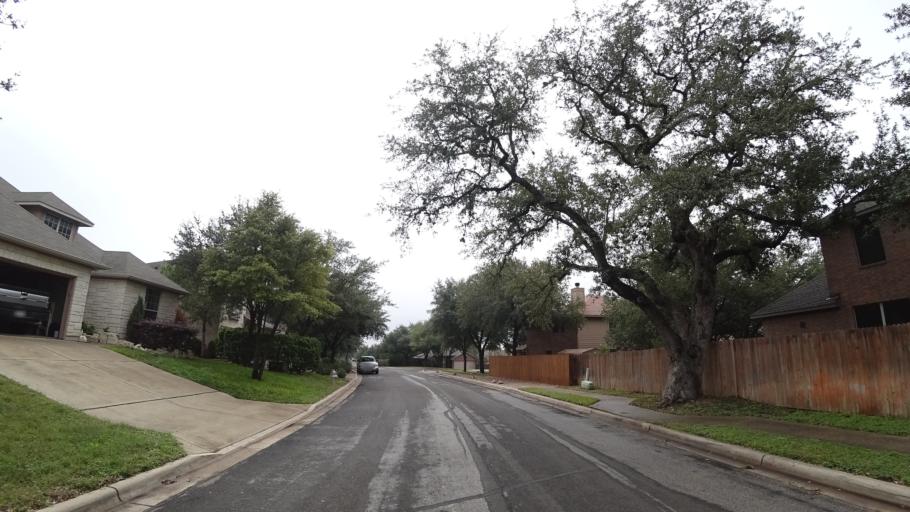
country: US
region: Texas
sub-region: Travis County
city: Shady Hollow
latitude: 30.1909
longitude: -97.8714
